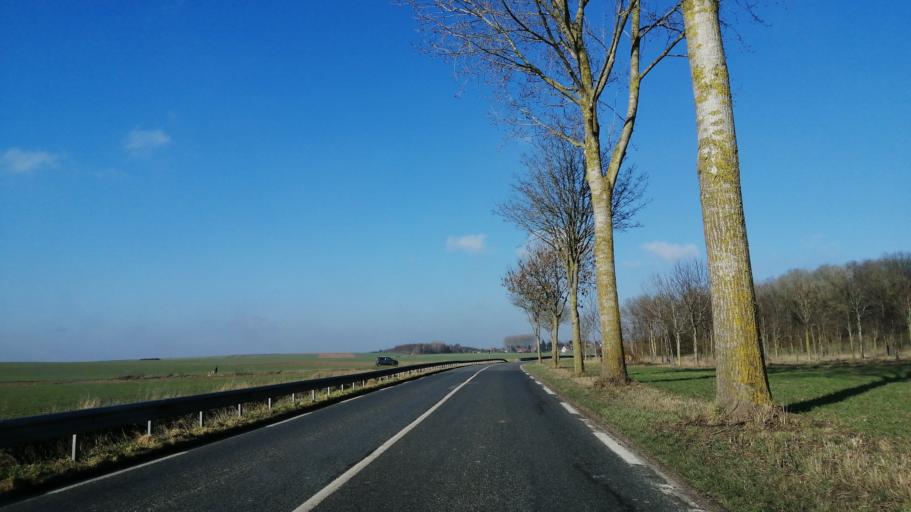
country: FR
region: Nord-Pas-de-Calais
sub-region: Departement du Pas-de-Calais
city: Mont-Saint-Eloi
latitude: 50.3649
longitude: 2.6521
